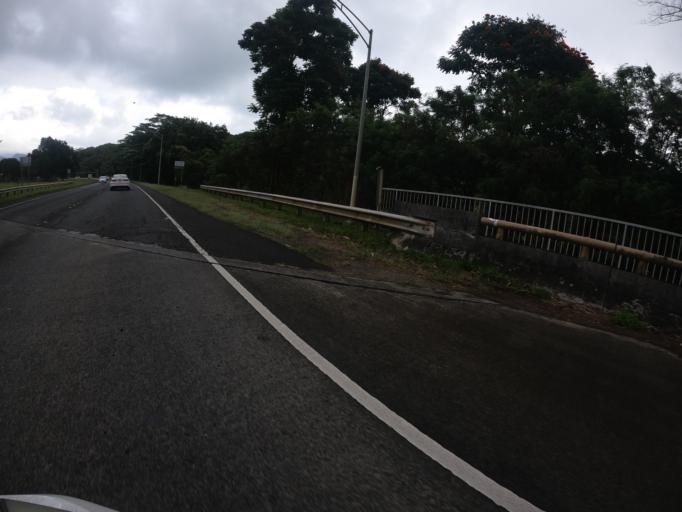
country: US
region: Hawaii
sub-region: Honolulu County
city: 'Ahuimanu
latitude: 21.4461
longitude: -157.8327
